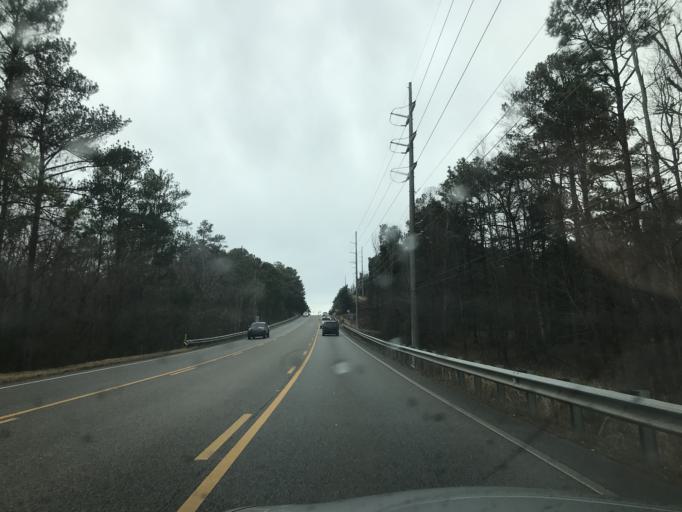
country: US
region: Alabama
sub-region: Shelby County
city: Indian Springs Village
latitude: 33.3761
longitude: -86.7316
